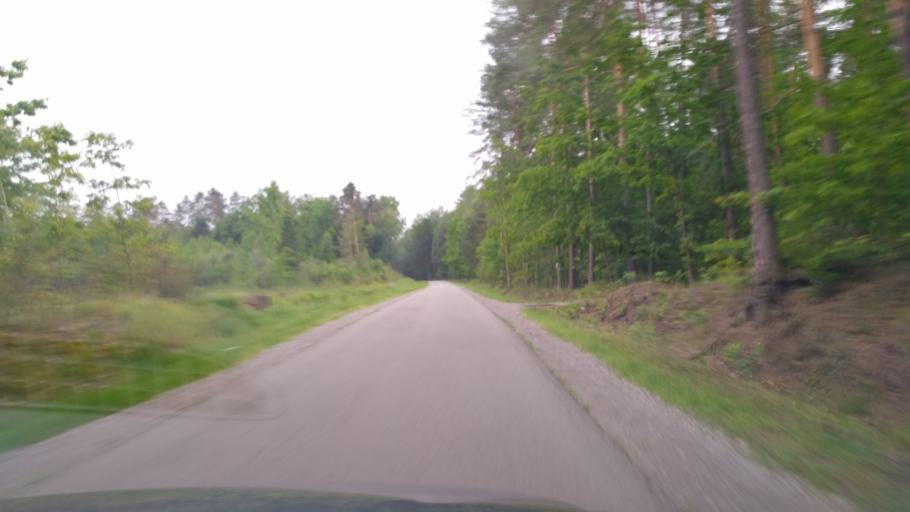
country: PL
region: Subcarpathian Voivodeship
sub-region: Powiat kolbuszowski
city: Niwiska
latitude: 50.2059
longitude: 21.6578
